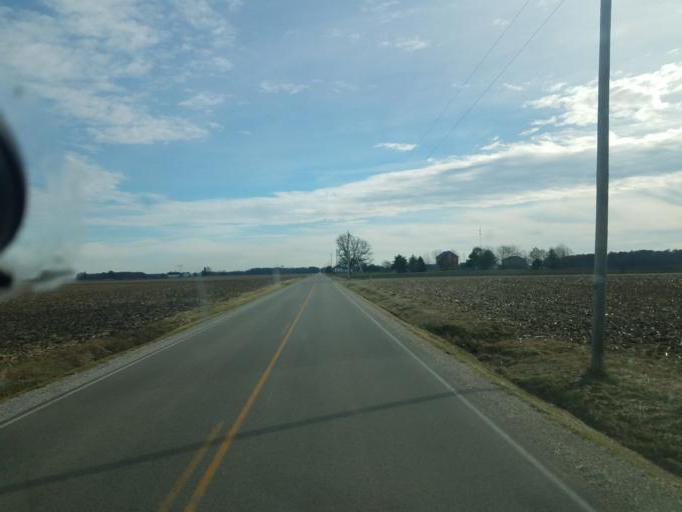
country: US
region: Ohio
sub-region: Crawford County
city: Galion
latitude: 40.7193
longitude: -82.9005
